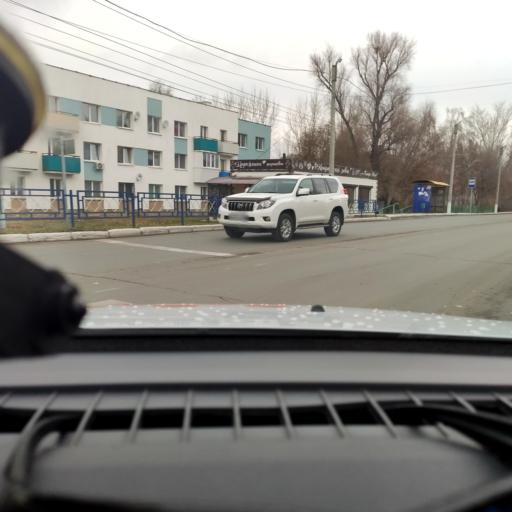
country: RU
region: Samara
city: Chapayevsk
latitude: 52.9731
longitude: 49.7080
